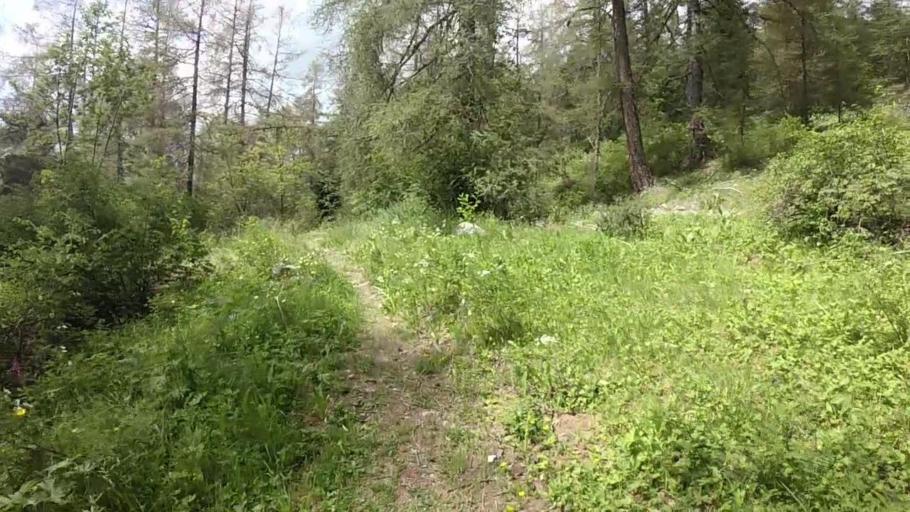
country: FR
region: Provence-Alpes-Cote d'Azur
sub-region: Departement des Alpes-de-Haute-Provence
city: Seyne-les-Alpes
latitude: 44.4085
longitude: 6.3681
